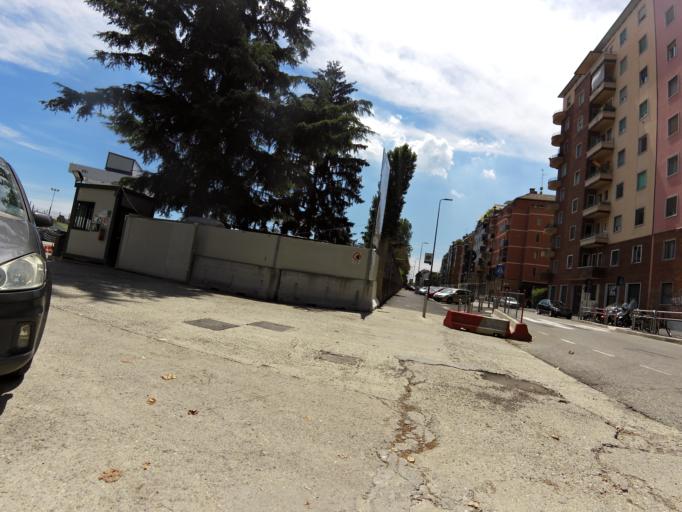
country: IT
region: Lombardy
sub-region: Citta metropolitana di Milano
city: Linate
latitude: 45.4668
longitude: 9.2352
